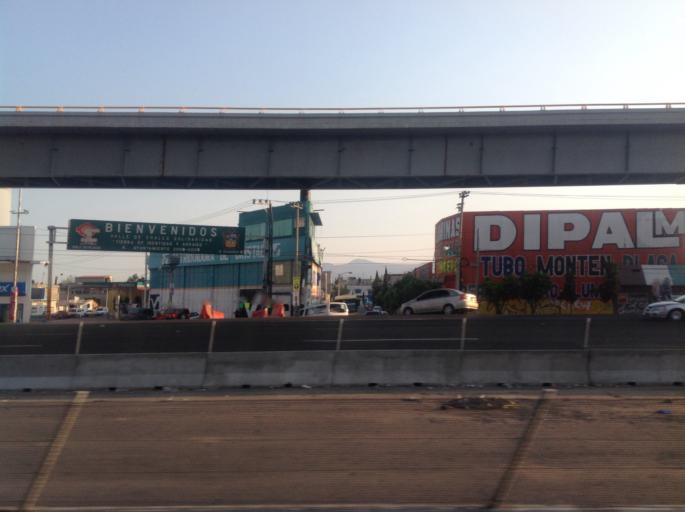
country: MX
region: Mexico
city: San Miguel Xico Viejo
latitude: 19.2906
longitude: -98.9181
